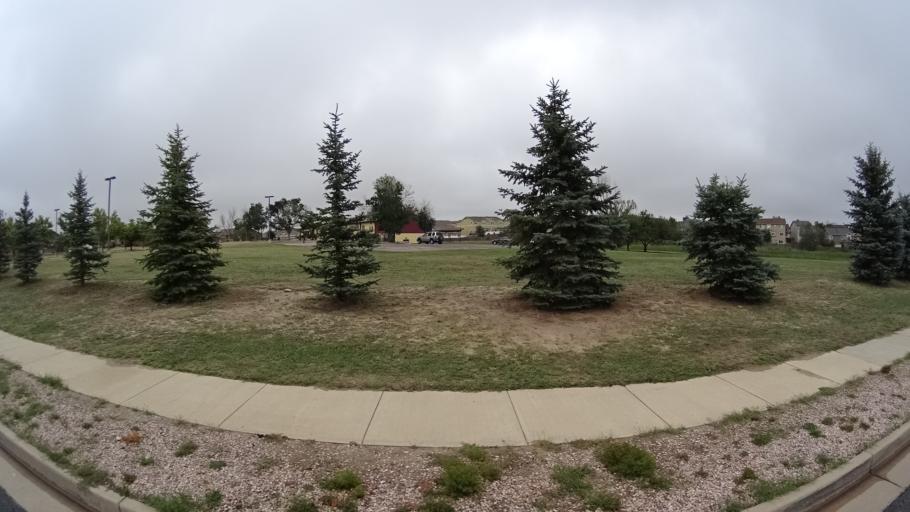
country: US
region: Colorado
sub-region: El Paso County
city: Cimarron Hills
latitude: 38.9271
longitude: -104.7282
